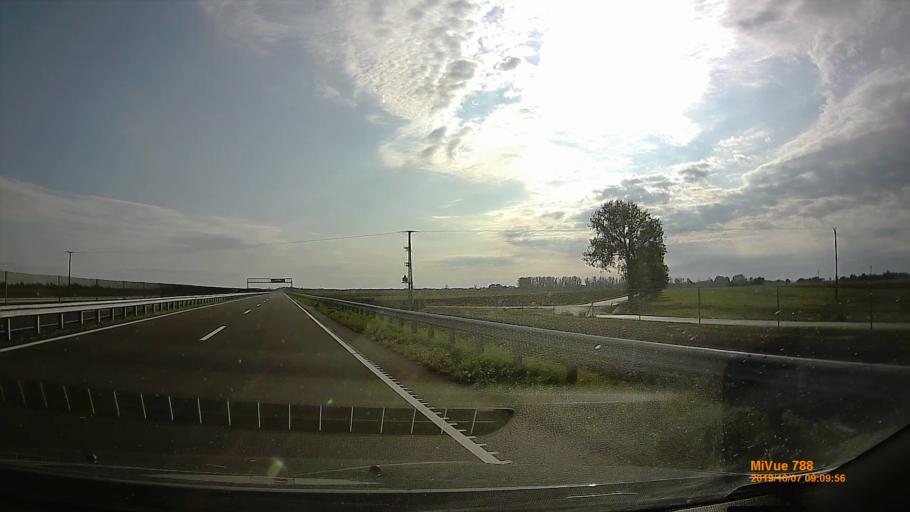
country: HU
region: Bekes
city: Szarvas
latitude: 46.8138
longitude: 20.6502
